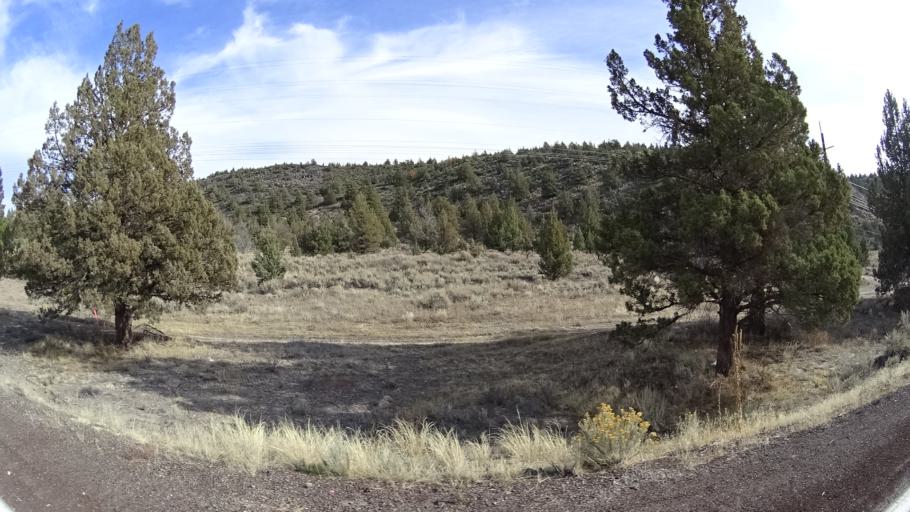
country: US
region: California
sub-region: Siskiyou County
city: Weed
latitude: 41.5239
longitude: -122.3657
